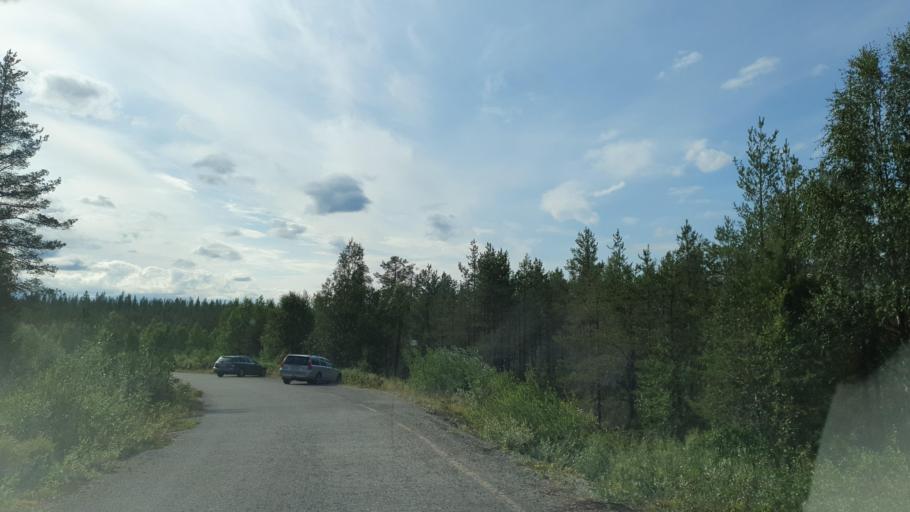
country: FI
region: Lapland
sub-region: Tunturi-Lappi
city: Muonio
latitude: 67.7072
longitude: 24.1281
